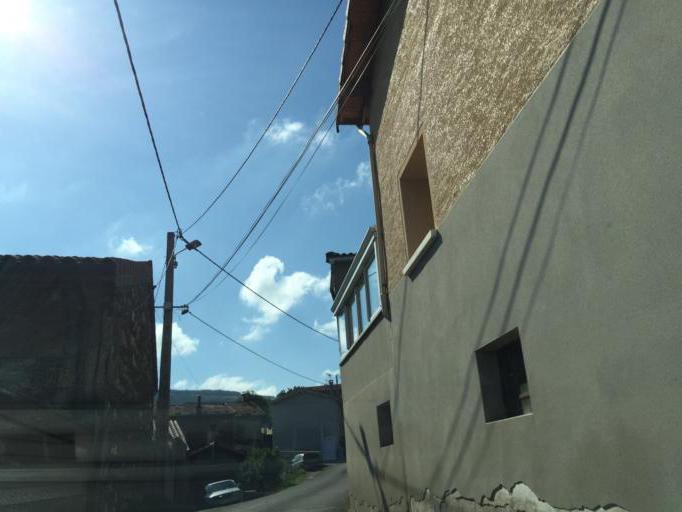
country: FR
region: Rhone-Alpes
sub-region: Departement de la Loire
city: Saint-Chamond
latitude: 45.4611
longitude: 4.5393
